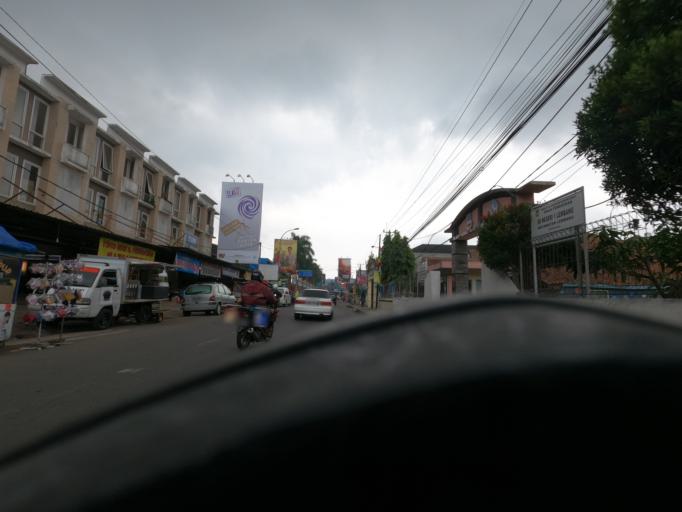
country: ID
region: West Java
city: Lembang
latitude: -6.8156
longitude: 107.6227
